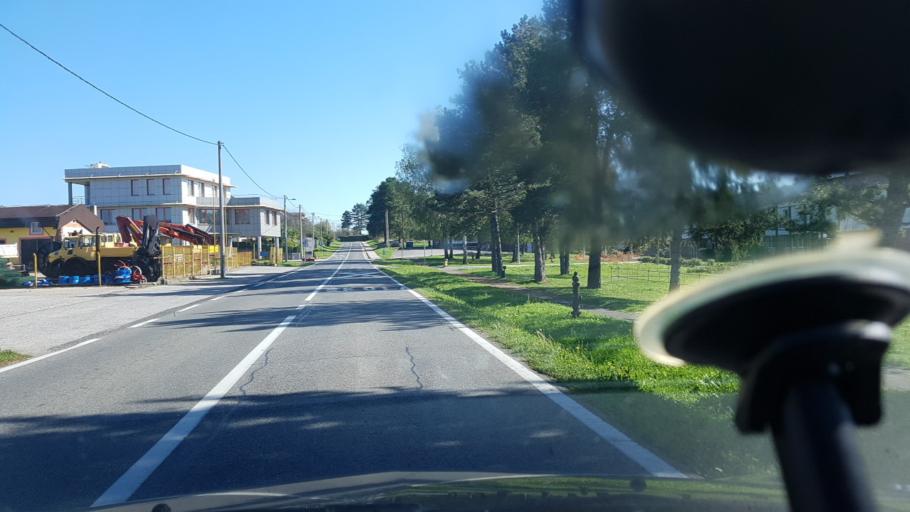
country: HR
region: Zagrebacka
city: Kriz
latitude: 45.7093
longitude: 16.4757
